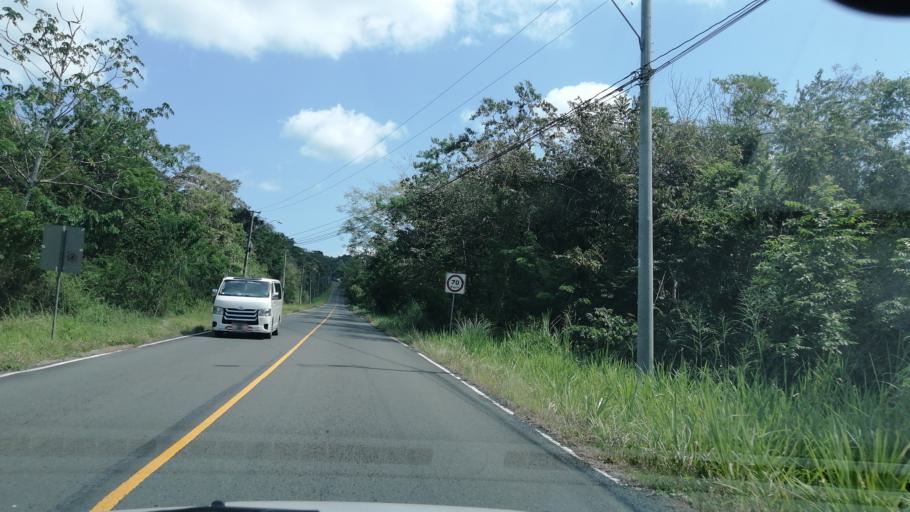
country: PA
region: Panama
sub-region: Distrito de Panama
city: Ancon
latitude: 8.9023
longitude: -79.5734
